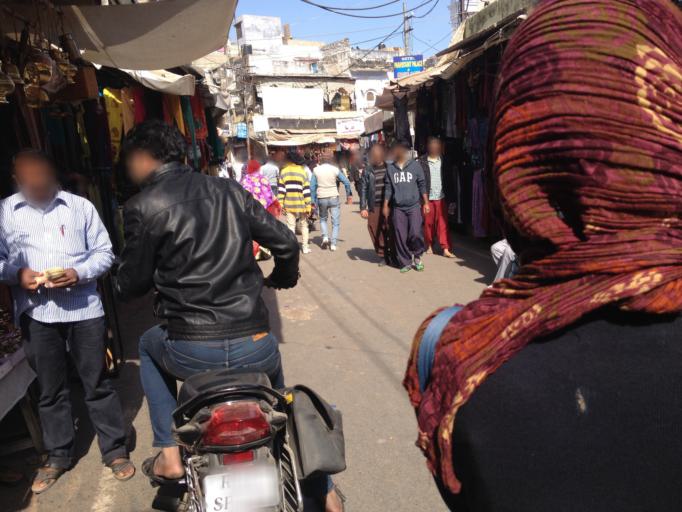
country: IN
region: Rajasthan
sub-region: Ajmer
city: Pushkar
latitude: 26.4887
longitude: 74.5522
